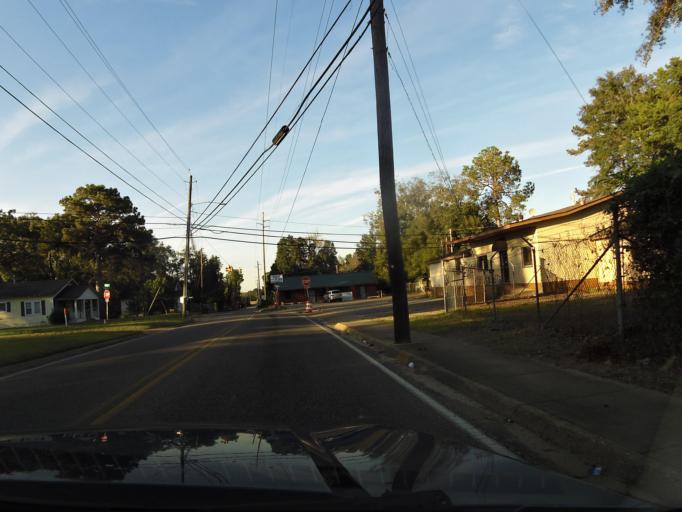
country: US
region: Alabama
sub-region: Houston County
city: Dothan
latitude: 31.2342
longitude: -85.3829
